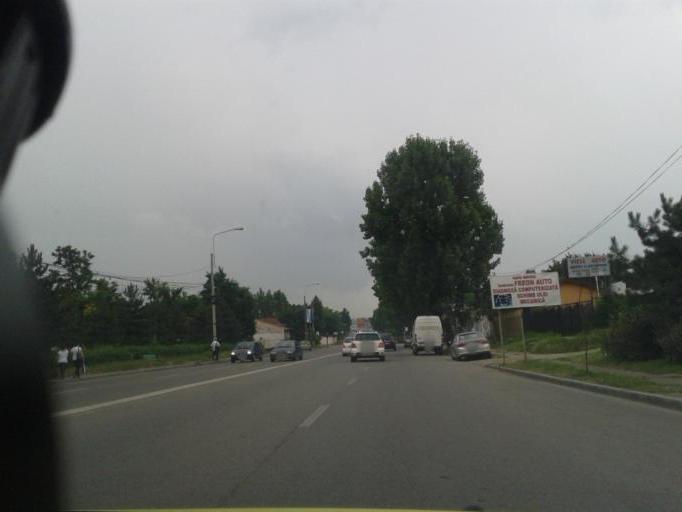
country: RO
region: Prahova
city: Ploiesti
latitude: 44.9523
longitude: 26.0441
